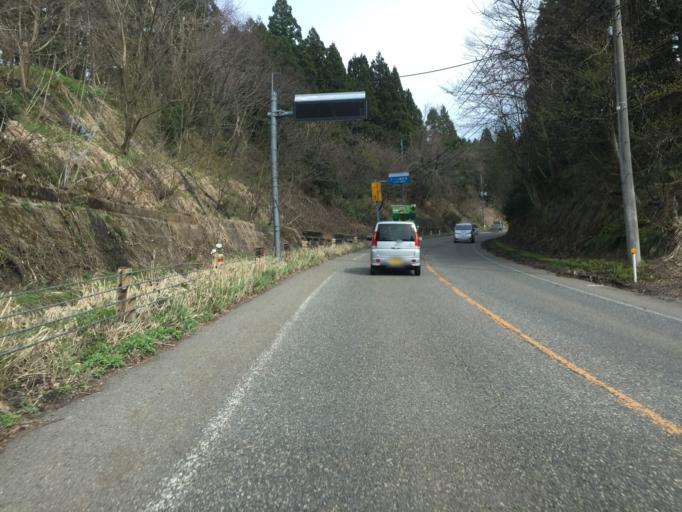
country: JP
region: Niigata
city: Nagaoka
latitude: 37.4546
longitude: 138.8996
